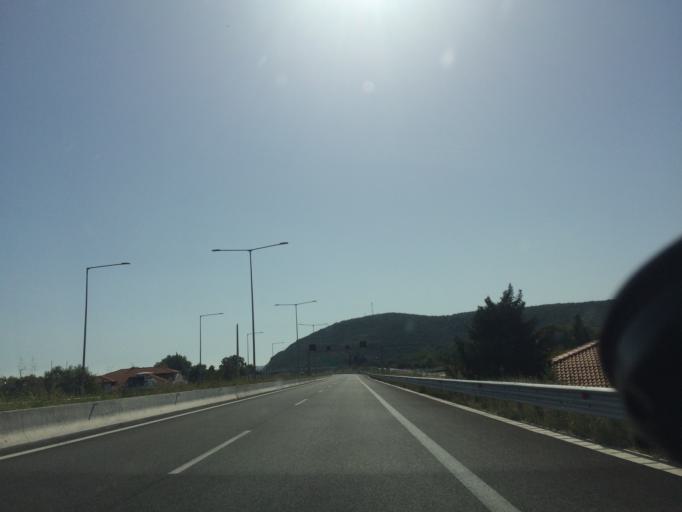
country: GR
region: Thessaly
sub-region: Nomos Larisis
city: Pyrgetos
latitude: 39.9823
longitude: 22.6178
